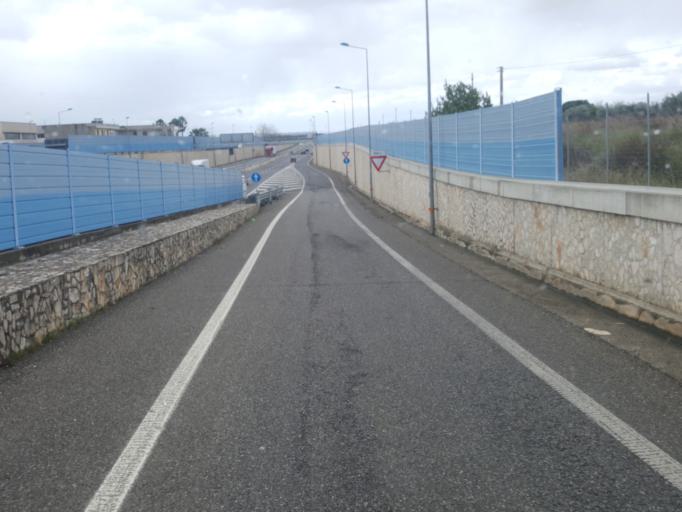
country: IT
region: Basilicate
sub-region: Provincia di Matera
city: Scanzano Jonico
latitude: 40.2458
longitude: 16.6965
